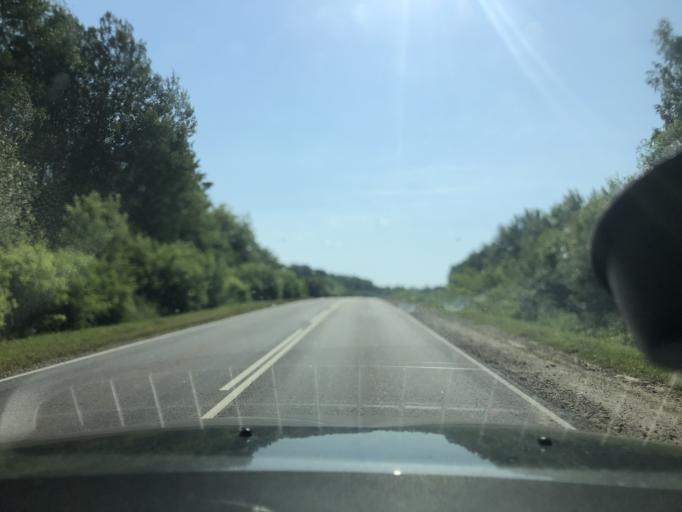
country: RU
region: Tula
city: Dubna
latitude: 54.1289
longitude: 37.0526
